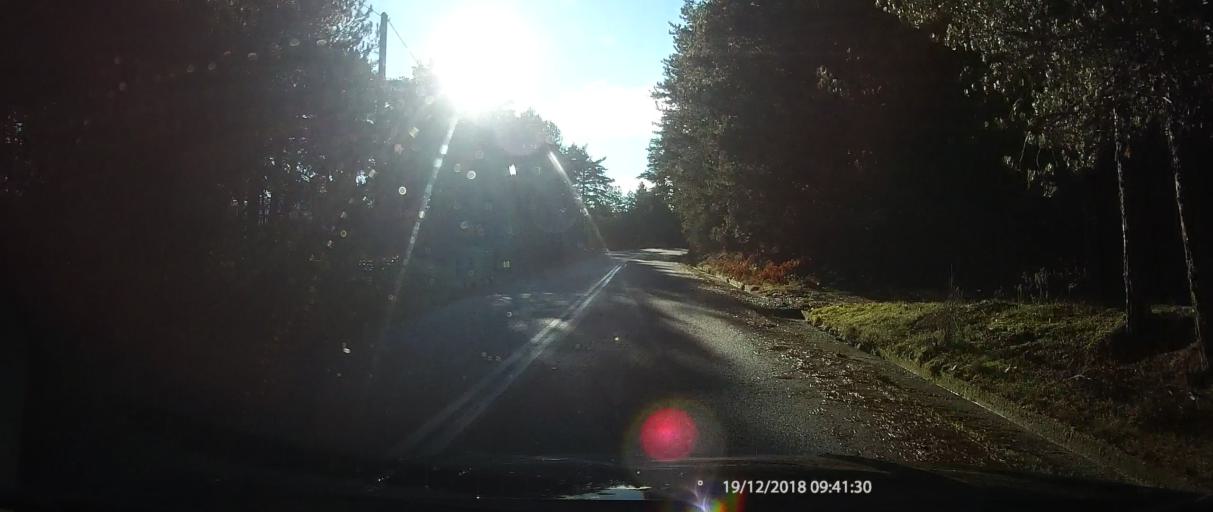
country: GR
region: Peloponnese
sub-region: Nomos Messinias
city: Paralia Vergas
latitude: 37.0712
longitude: 22.2700
